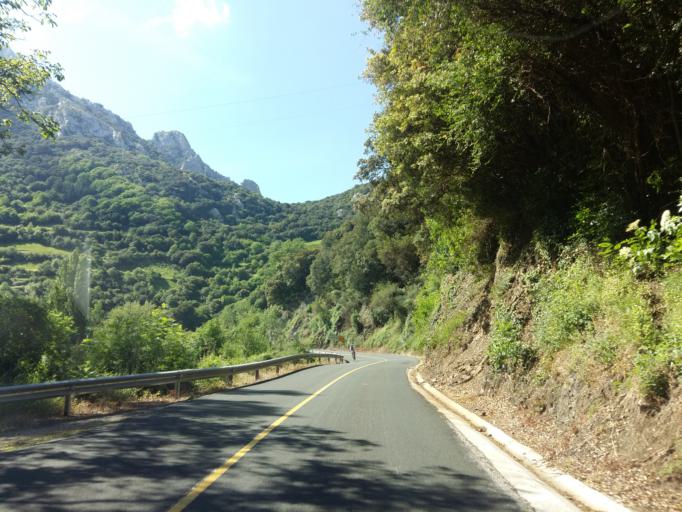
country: ES
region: Cantabria
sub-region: Provincia de Cantabria
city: Potes
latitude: 43.2153
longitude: -4.5926
